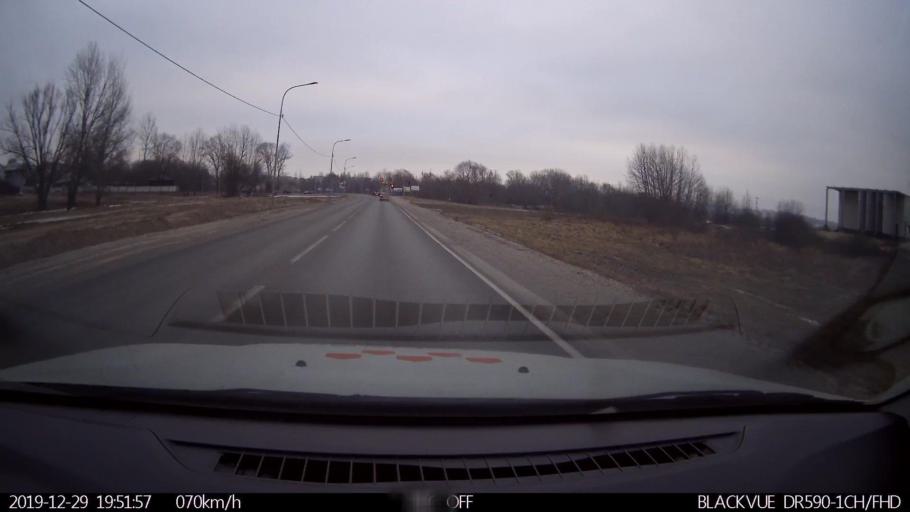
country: RU
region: Nizjnij Novgorod
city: Bor
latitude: 56.3571
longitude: 44.0487
